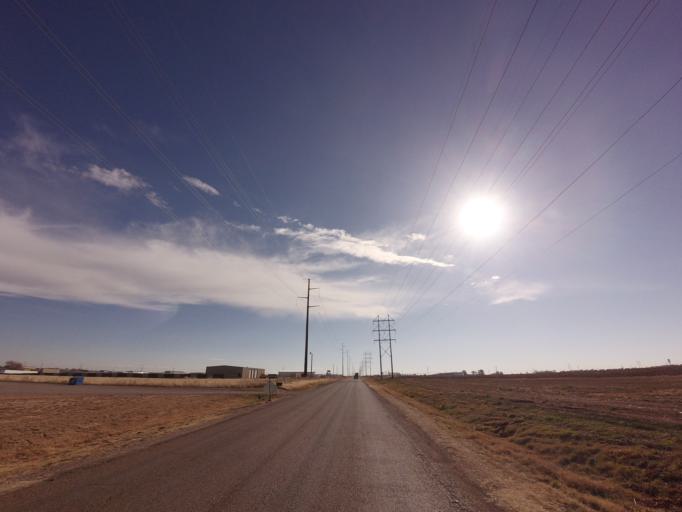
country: US
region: New Mexico
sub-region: Curry County
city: Clovis
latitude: 34.4029
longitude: -103.1433
